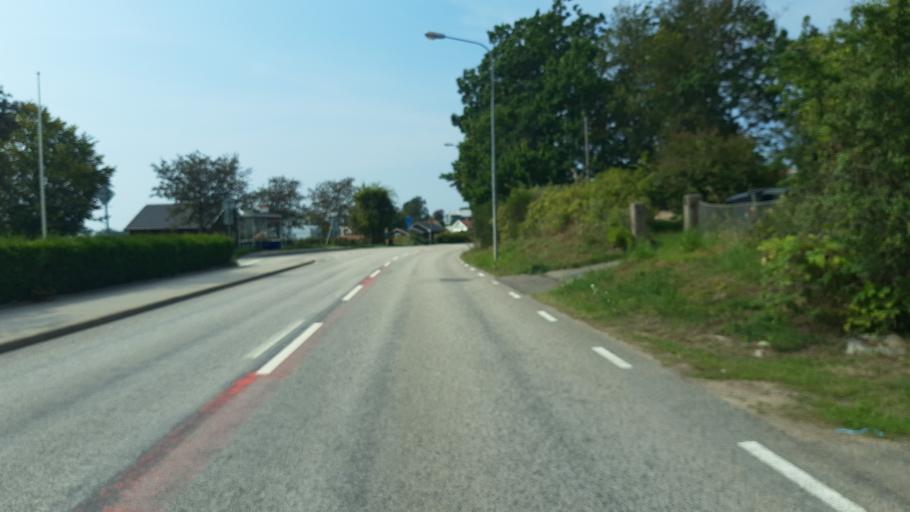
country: SE
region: Blekinge
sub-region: Ronneby Kommun
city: Ronneby
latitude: 56.1730
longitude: 15.2813
